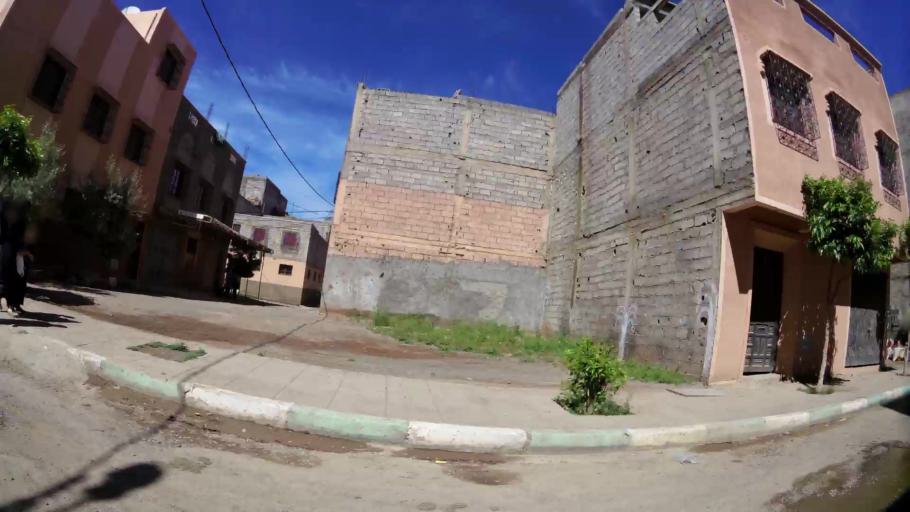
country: MA
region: Marrakech-Tensift-Al Haouz
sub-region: Marrakech
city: Marrakesh
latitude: 31.6426
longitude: -8.1145
